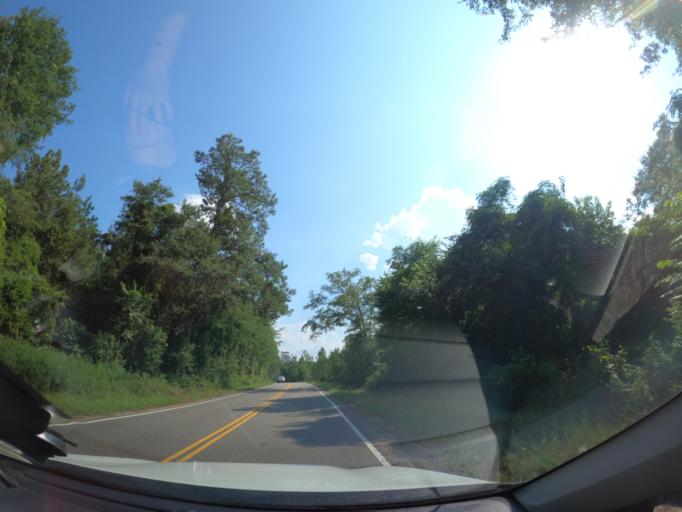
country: US
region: South Carolina
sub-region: Barnwell County
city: Williston
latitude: 33.5643
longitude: -81.4816
